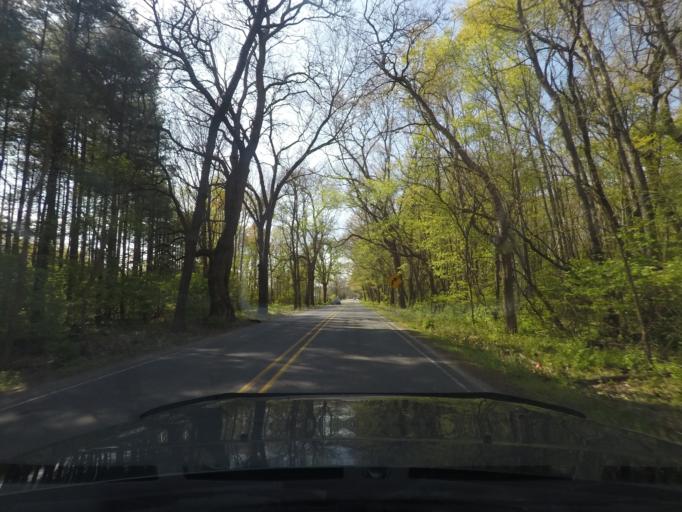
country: US
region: Indiana
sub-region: Elkhart County
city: Elkhart
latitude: 41.7113
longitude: -86.0253
